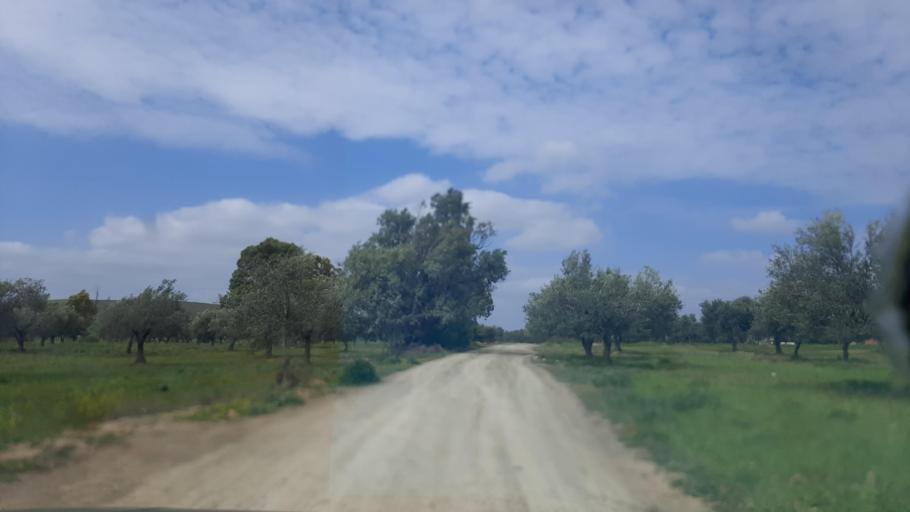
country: TN
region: Tunis
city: Oued Lill
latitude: 36.6888
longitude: 9.9947
